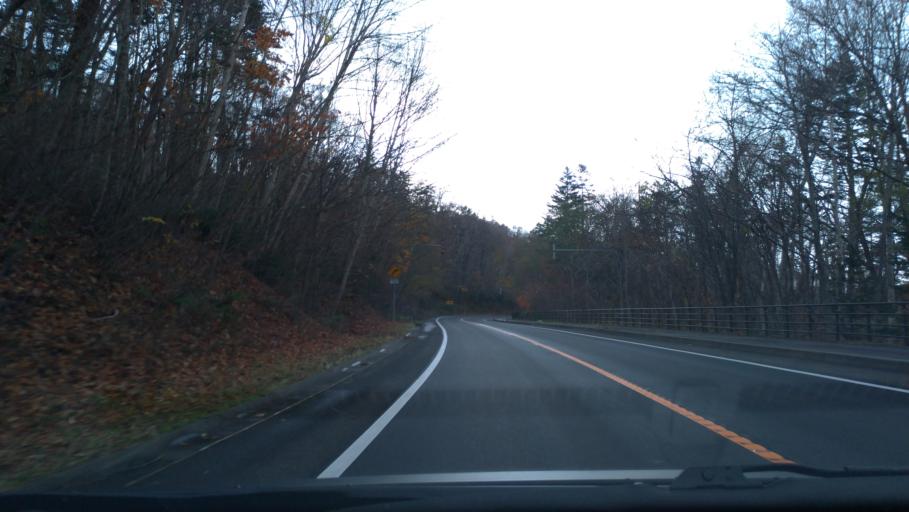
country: JP
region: Hokkaido
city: Shiraoi
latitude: 42.7342
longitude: 141.3456
